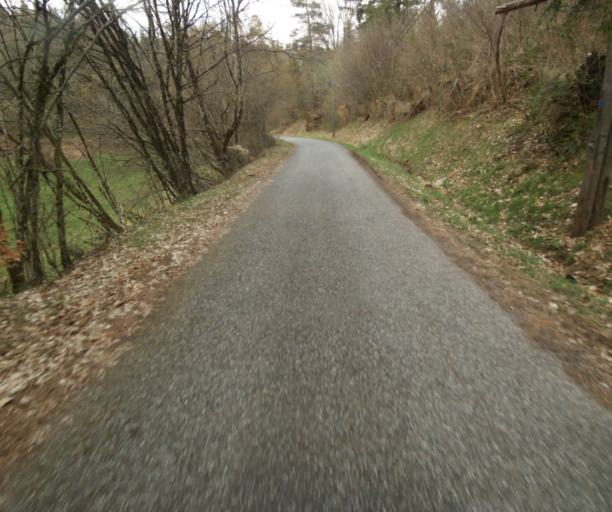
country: FR
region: Limousin
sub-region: Departement de la Correze
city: Correze
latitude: 45.2906
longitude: 1.9305
